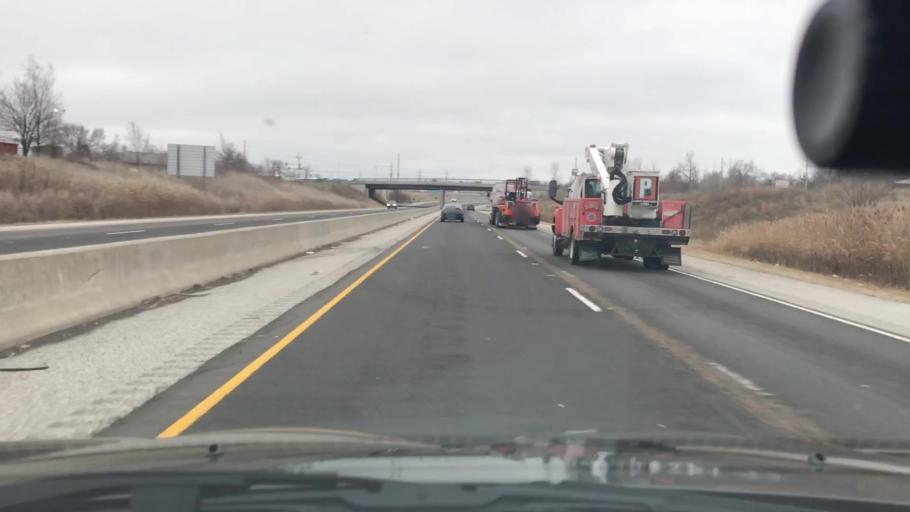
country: US
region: Illinois
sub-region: Madison County
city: Rosewood Heights
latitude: 38.8898
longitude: -90.0613
